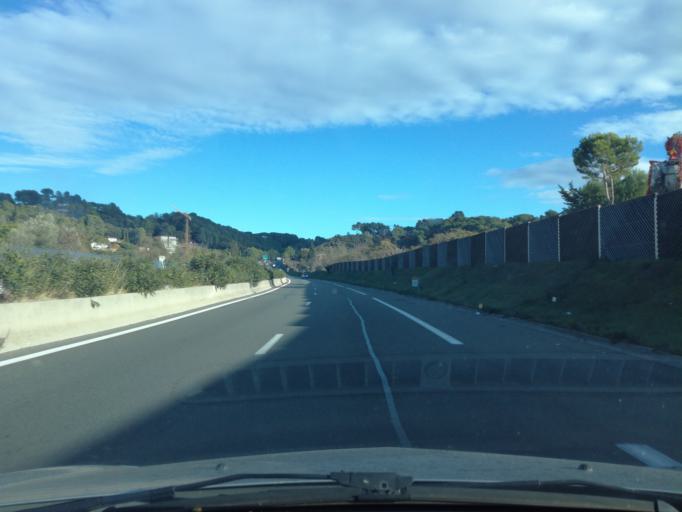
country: FR
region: Provence-Alpes-Cote d'Azur
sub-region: Departement des Alpes-Maritimes
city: Mouans-Sartoux
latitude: 43.6078
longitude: 6.9779
